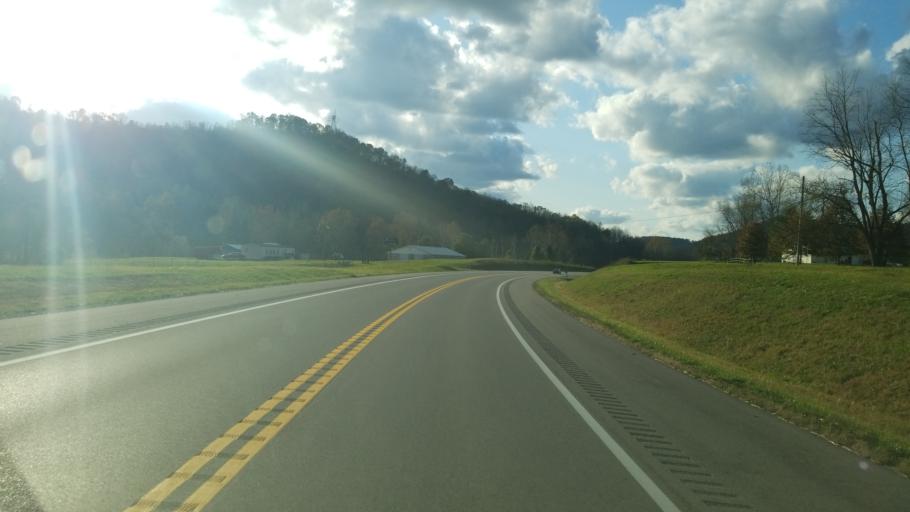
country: US
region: Kentucky
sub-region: Lewis County
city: Vanceburg
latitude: 38.5821
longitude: -83.3611
